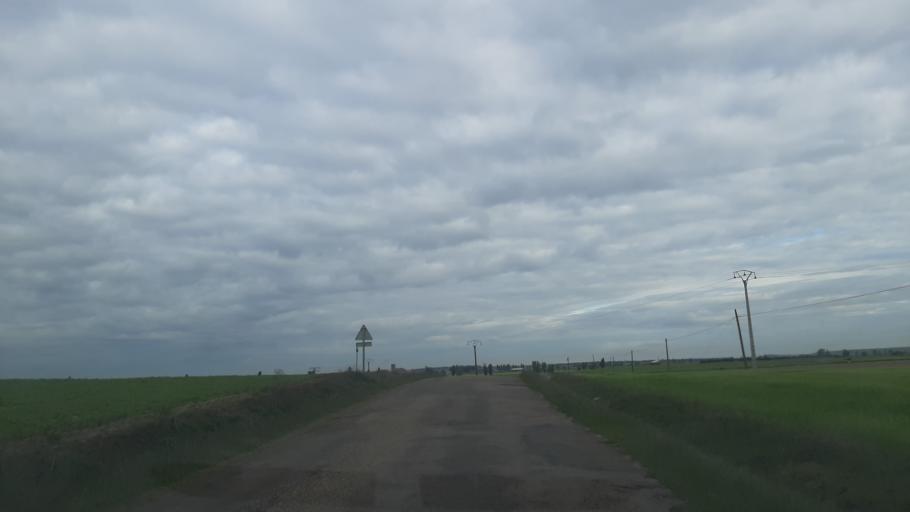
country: ES
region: Castille and Leon
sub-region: Provincia de Salamanca
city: Villaflores
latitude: 41.0754
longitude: -5.2147
